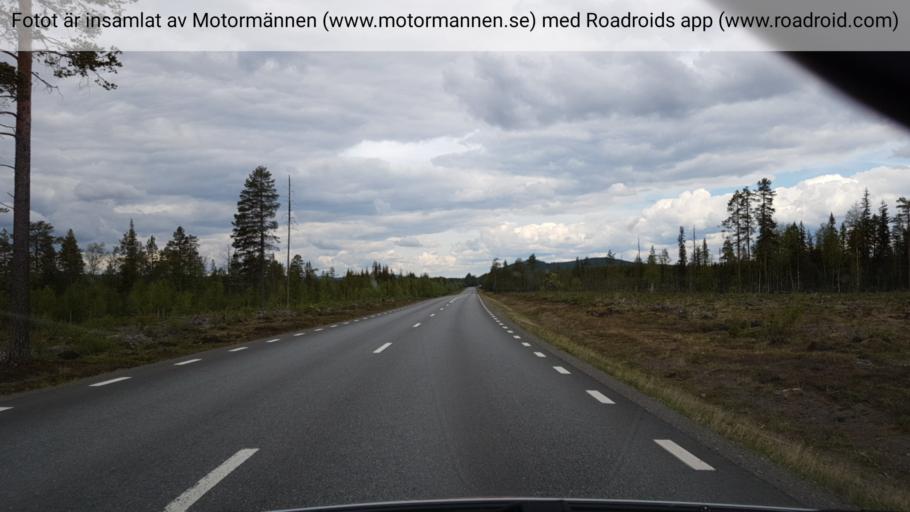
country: SE
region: Norrbotten
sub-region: Arvidsjaurs Kommun
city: Arvidsjaur
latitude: 65.5005
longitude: 19.2973
